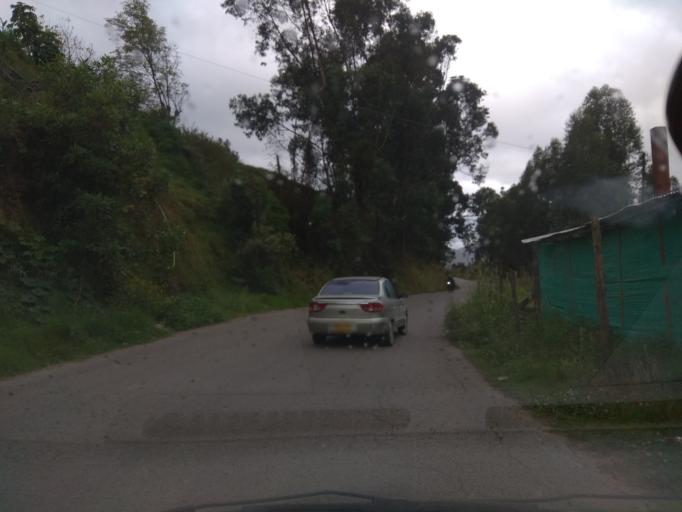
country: CO
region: Boyaca
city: Topaga
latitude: 5.7563
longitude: -72.8522
